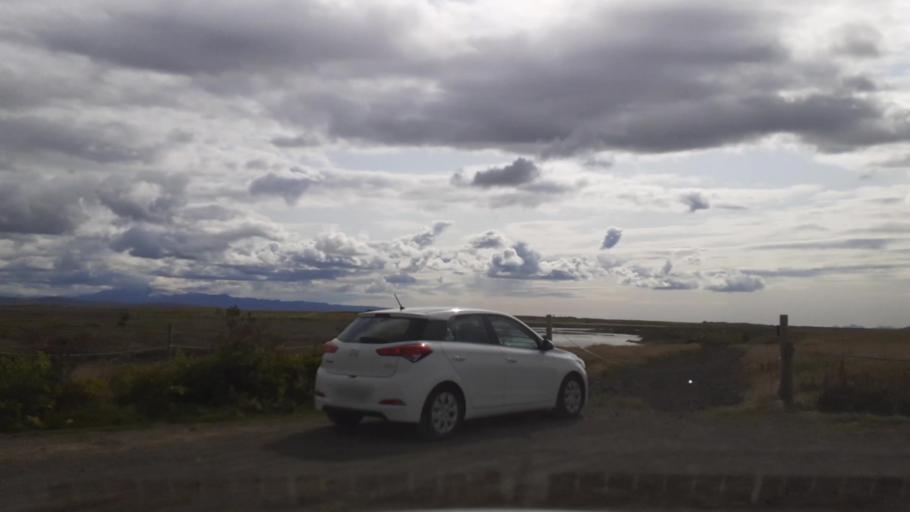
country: IS
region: South
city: Vestmannaeyjar
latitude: 63.8187
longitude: -20.4197
